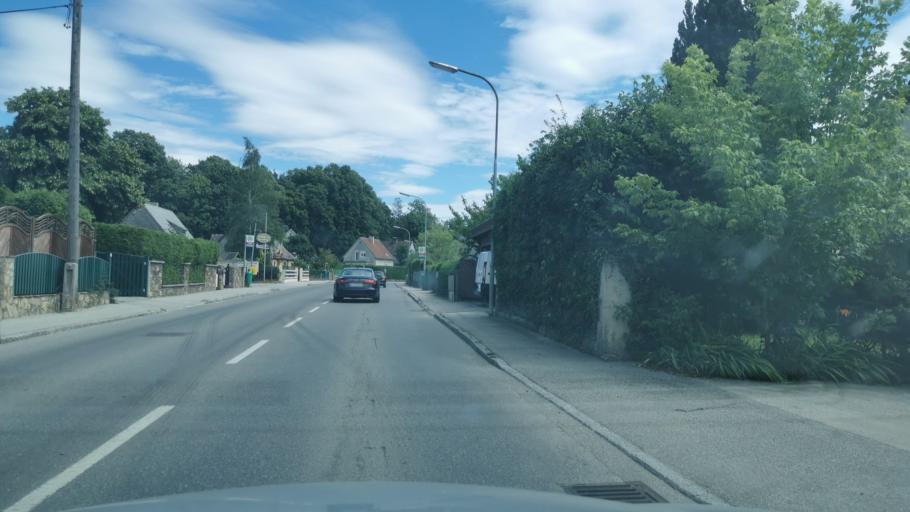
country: AT
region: Lower Austria
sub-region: Sankt Polten Stadt
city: Sankt Poelten
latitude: 48.1713
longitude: 15.6338
